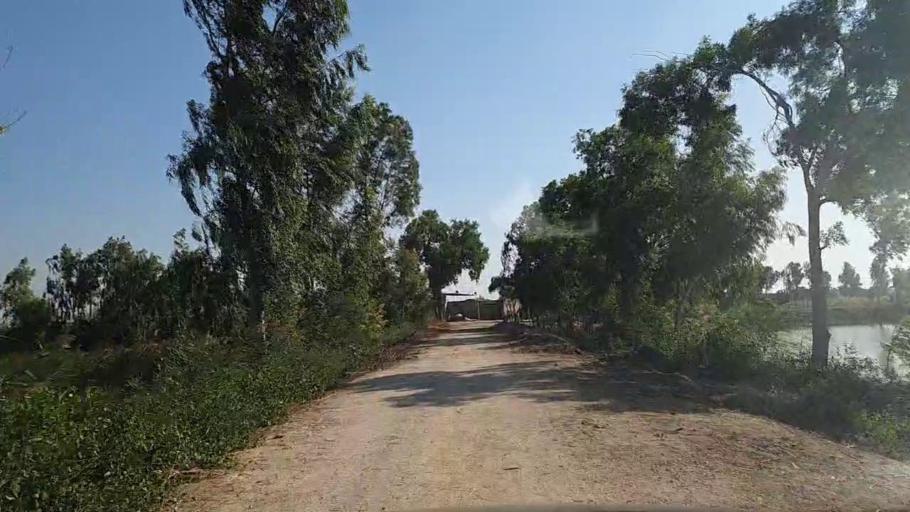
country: PK
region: Sindh
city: Mirpur Batoro
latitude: 24.7277
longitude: 68.2338
